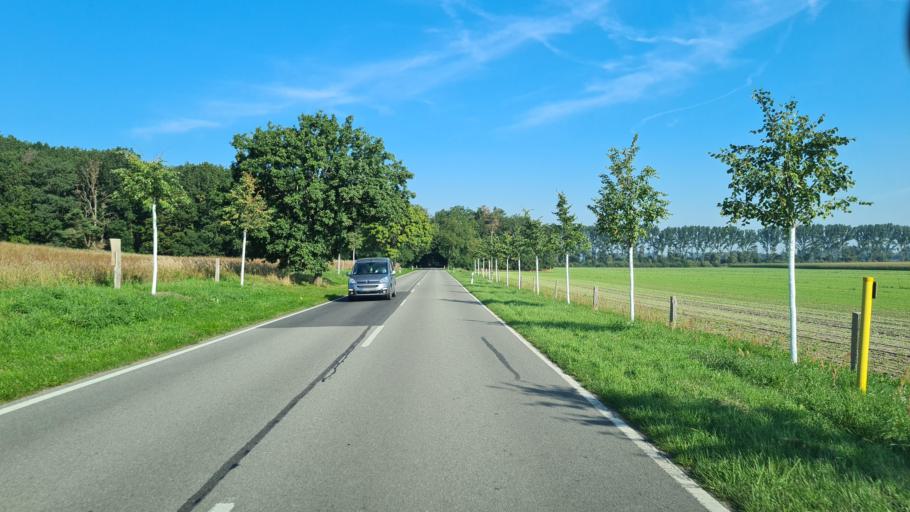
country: DE
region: Brandenburg
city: Pessin
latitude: 52.6990
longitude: 12.6482
